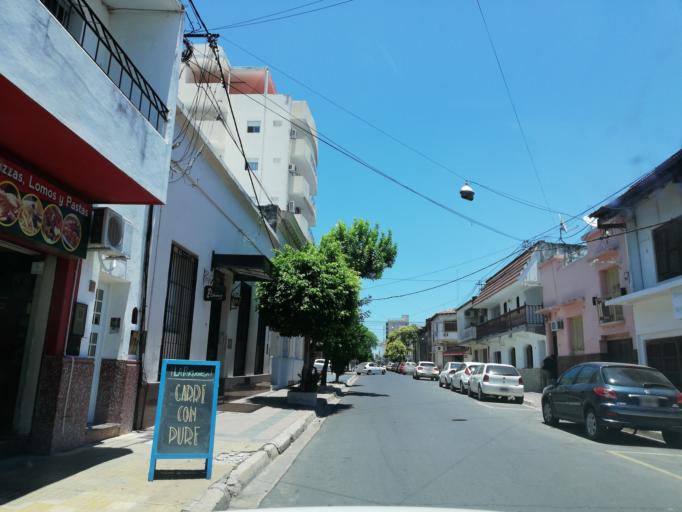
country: AR
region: Corrientes
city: Corrientes
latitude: -27.4629
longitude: -58.8312
